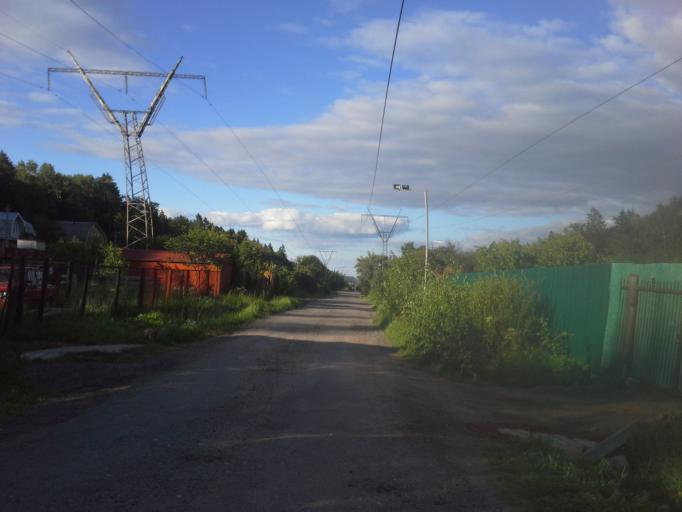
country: RU
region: Moskovskaya
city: Kievskij
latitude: 55.4467
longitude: 36.8284
